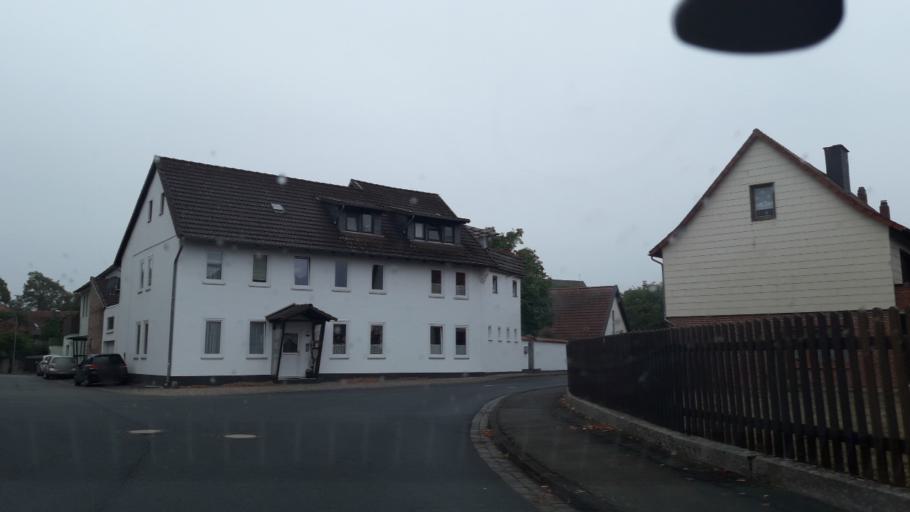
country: DE
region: Lower Saxony
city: Vienenburg
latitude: 51.9613
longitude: 10.5885
